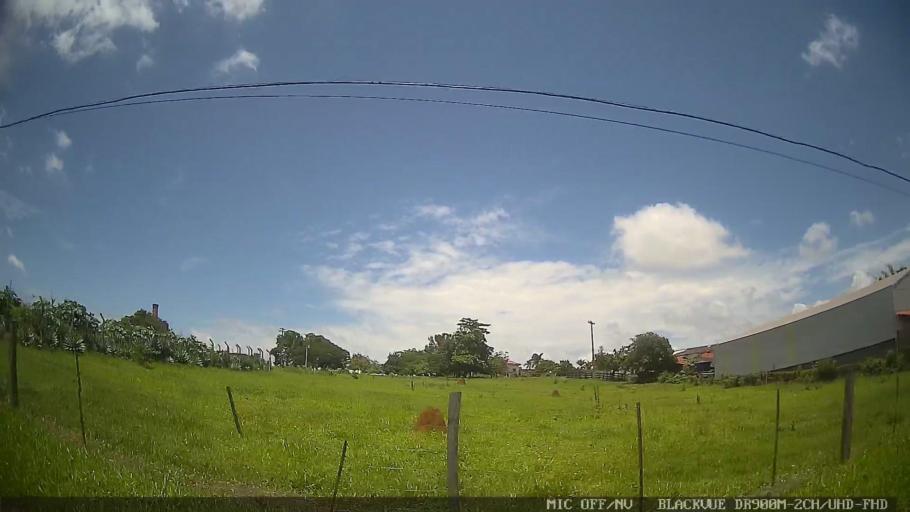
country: BR
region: Sao Paulo
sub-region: Laranjal Paulista
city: Laranjal Paulista
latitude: -23.0373
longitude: -47.8547
